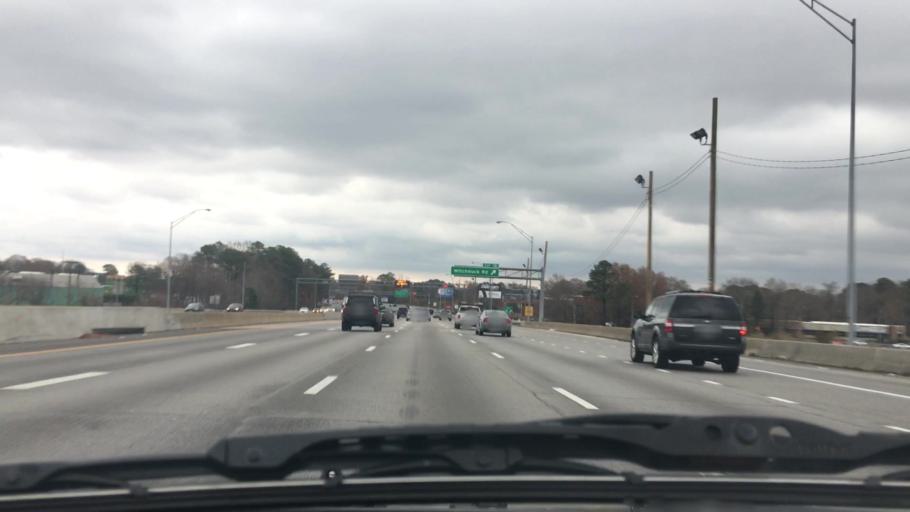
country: US
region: Virginia
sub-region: City of Chesapeake
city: Chesapeake
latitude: 36.8388
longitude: -76.1599
